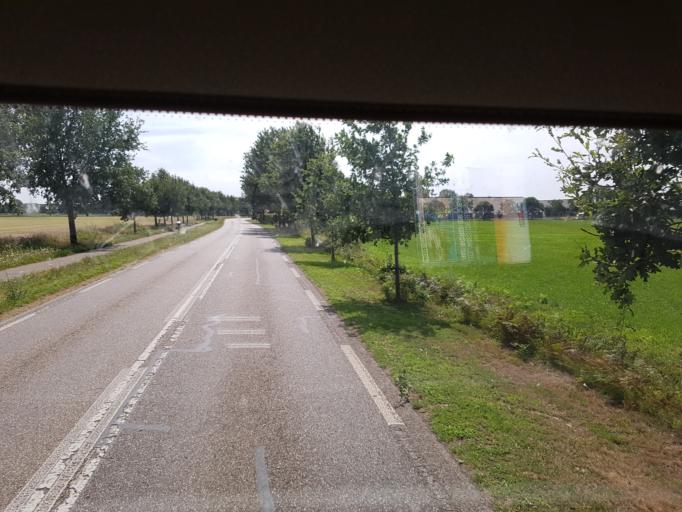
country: NL
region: Limburg
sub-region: Gemeente Leudal
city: Kelpen-Oler
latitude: 51.1833
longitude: 5.8187
